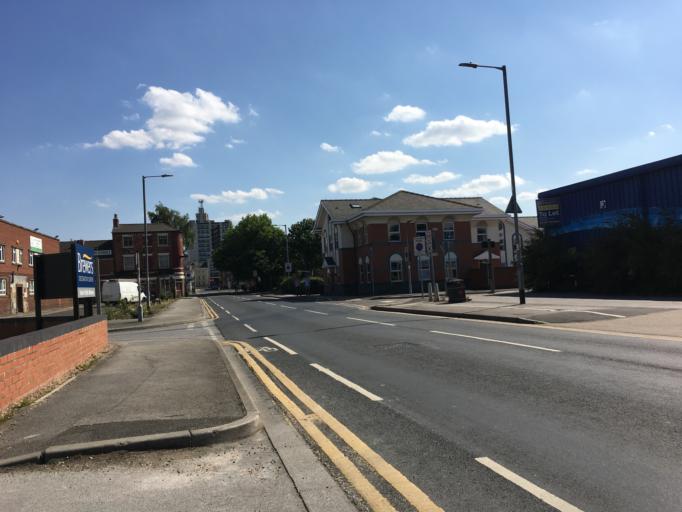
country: GB
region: England
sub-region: City of Kingston upon Hull
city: Hull
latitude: 53.7497
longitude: -0.3406
